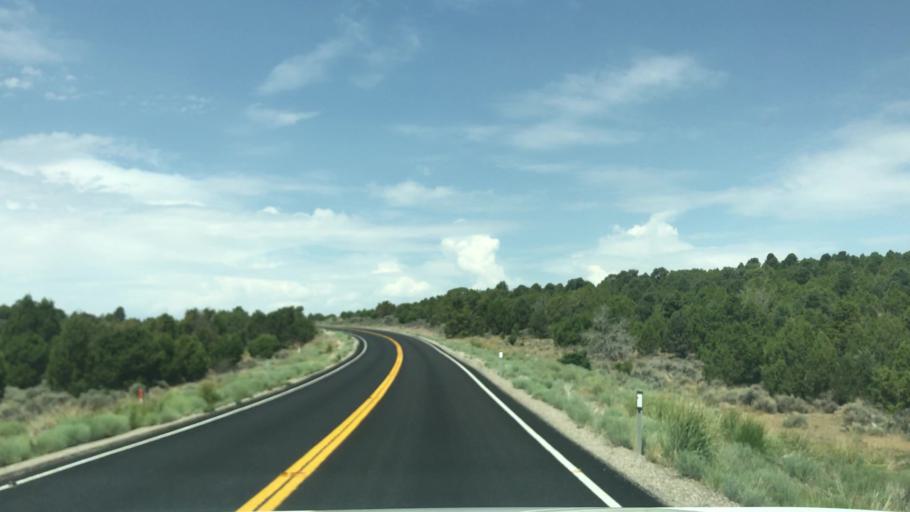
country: US
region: Nevada
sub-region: Eureka County
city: Eureka
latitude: 39.3959
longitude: -115.4633
